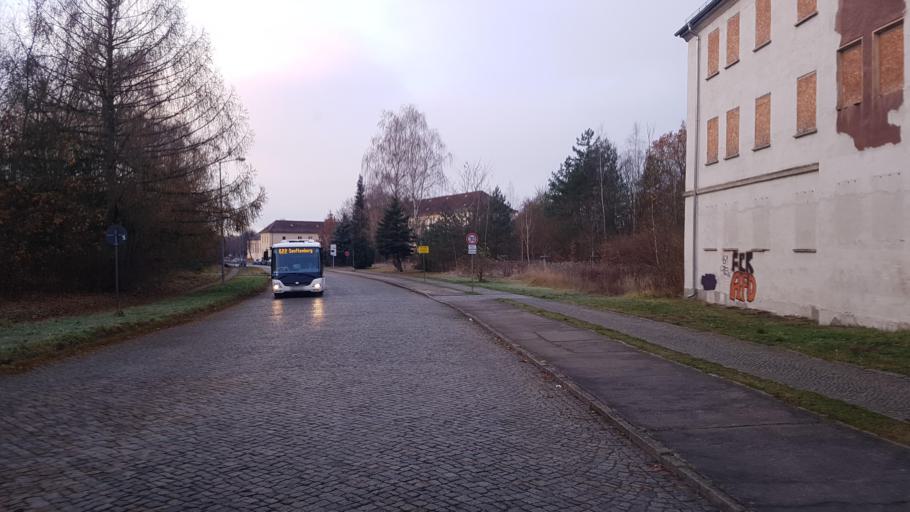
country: DE
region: Brandenburg
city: Lauchhammer
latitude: 51.4997
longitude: 13.7470
